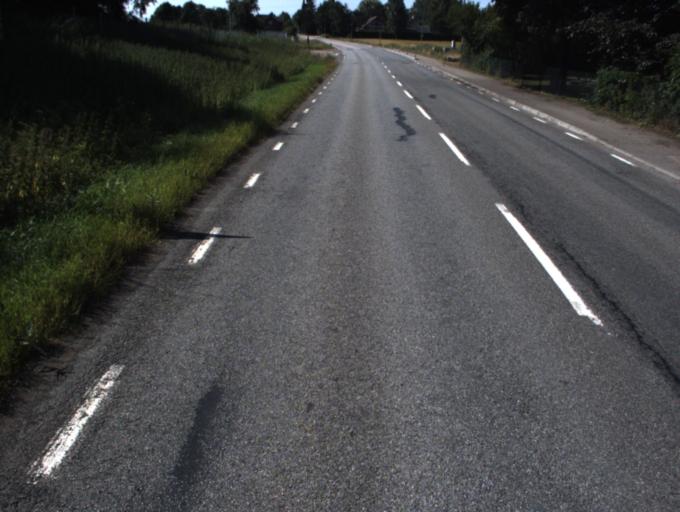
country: SE
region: Skane
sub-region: Angelholms Kommun
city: Strovelstorp
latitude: 56.1336
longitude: 12.8114
